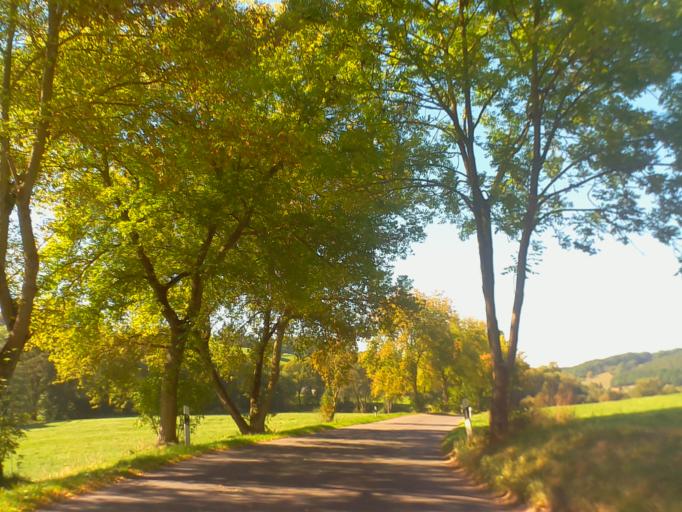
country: DE
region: Thuringia
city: Kleinebersdorf
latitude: 50.8223
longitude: 11.8283
